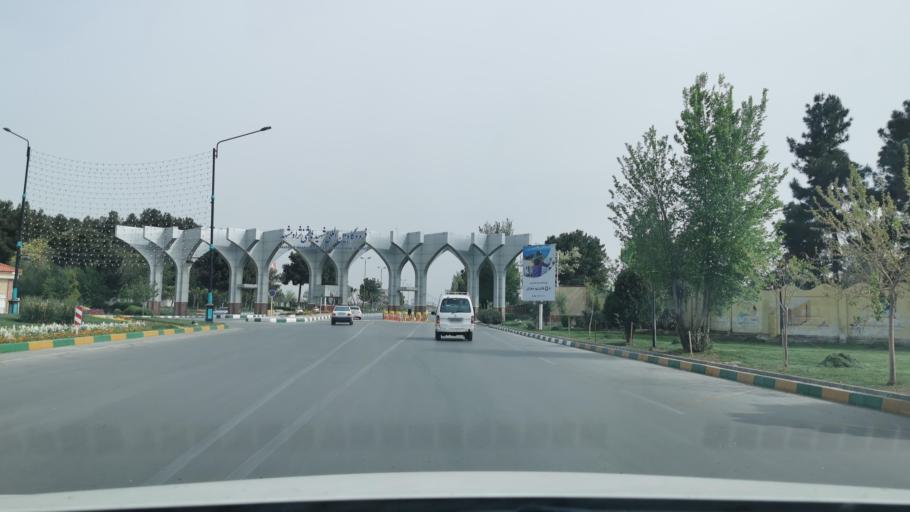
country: IR
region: Razavi Khorasan
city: Mashhad
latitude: 36.2422
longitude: 59.6243
